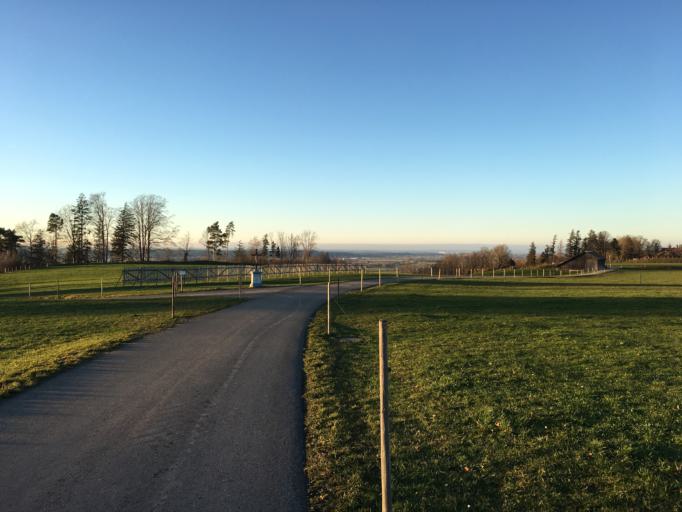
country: DE
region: Bavaria
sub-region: Swabia
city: Wolfertschwenden
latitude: 47.8737
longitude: 10.2774
